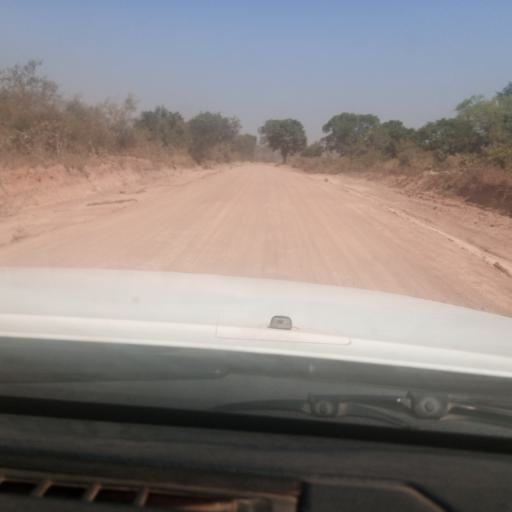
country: NG
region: Adamawa
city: Yola
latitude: 9.0968
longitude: 12.3899
